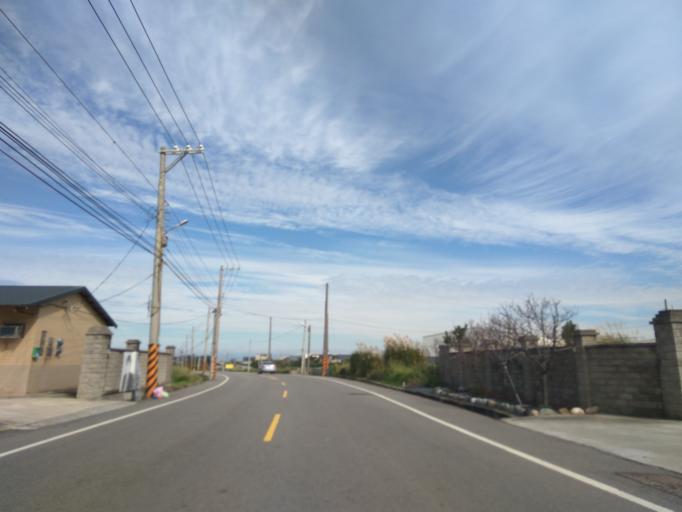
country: TW
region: Taiwan
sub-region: Hsinchu
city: Zhubei
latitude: 25.0145
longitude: 121.0702
